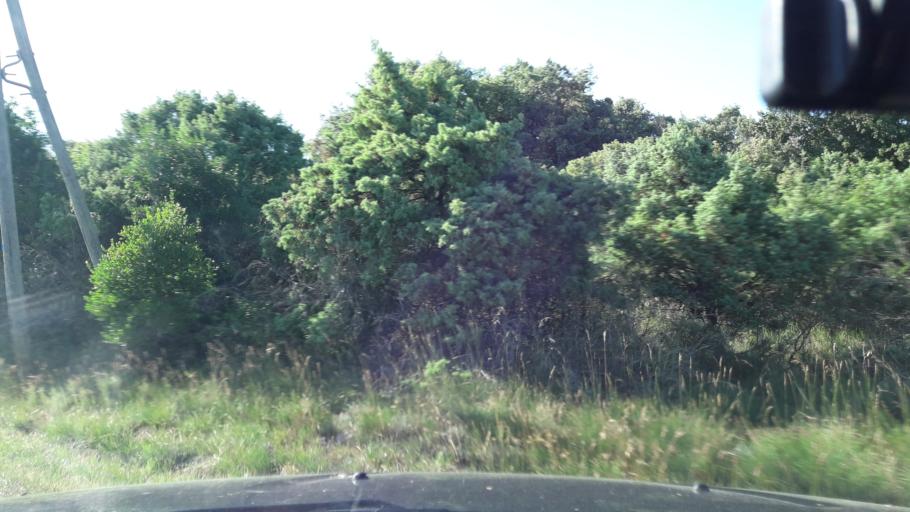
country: FR
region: Languedoc-Roussillon
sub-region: Departement du Gard
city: Saint-Julien-de-Peyrolas
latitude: 44.3657
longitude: 4.5246
